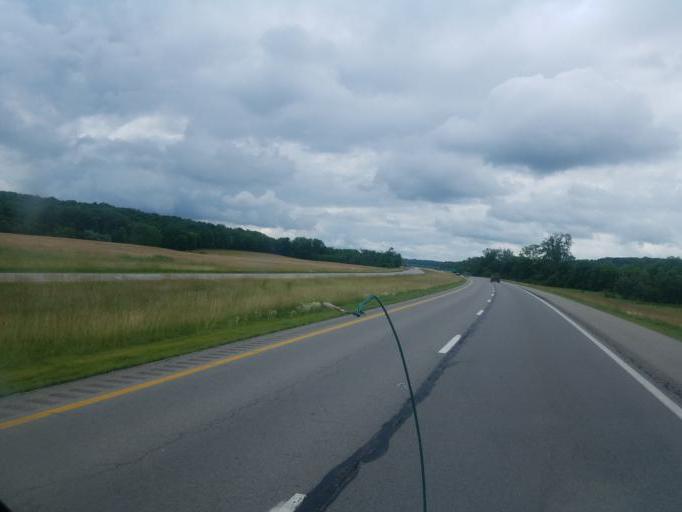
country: US
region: Ohio
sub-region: Logan County
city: Bellefontaine
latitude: 40.3281
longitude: -83.6764
